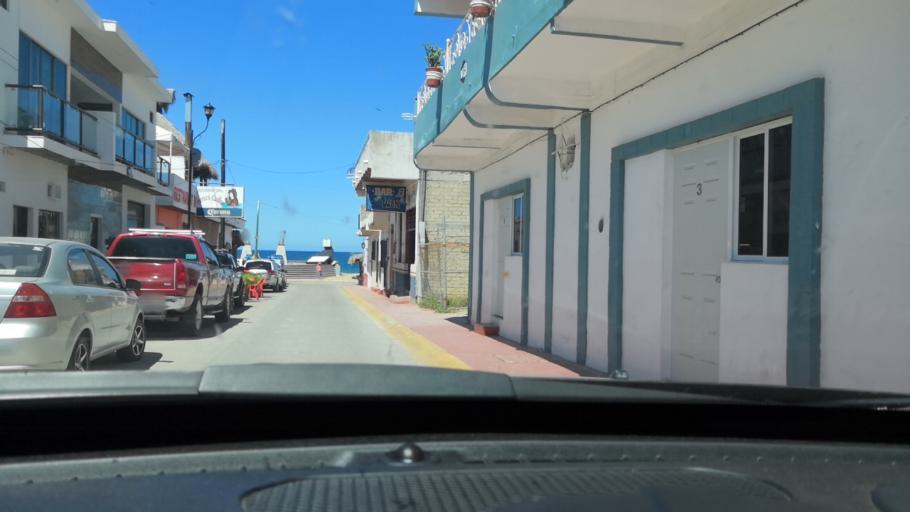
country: MX
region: Nayarit
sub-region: Compostela
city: Colonia Paraiso Escondido
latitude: 21.0417
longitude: -105.2499
